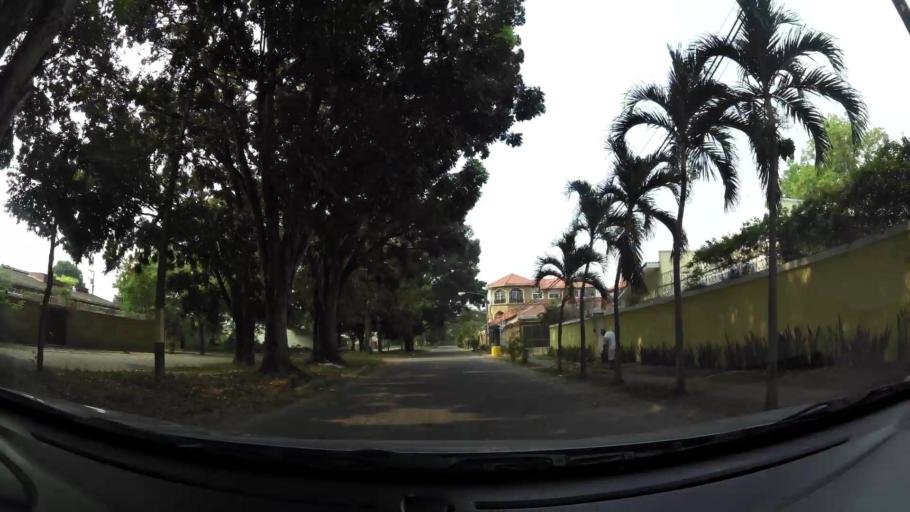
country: HN
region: Cortes
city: San Pedro Sula
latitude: 15.5259
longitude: -88.0275
